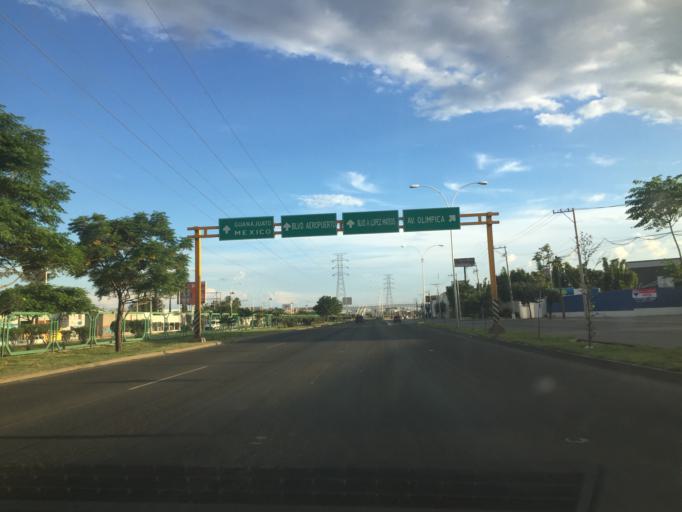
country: MX
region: Guanajuato
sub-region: Leon
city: Medina
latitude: 21.1087
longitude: -101.6243
